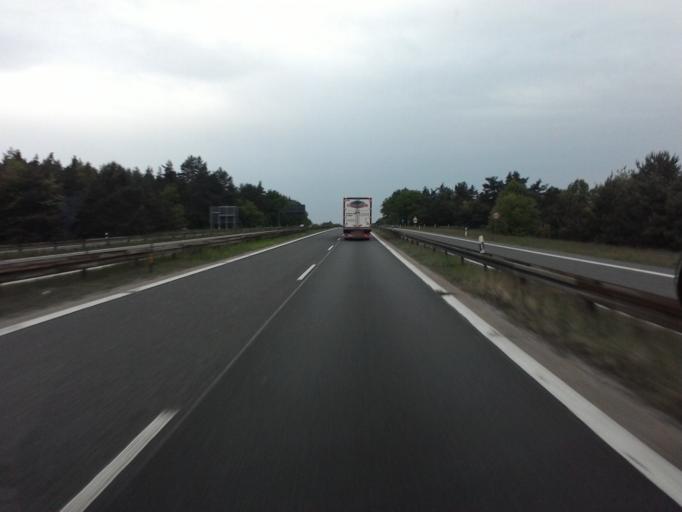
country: DE
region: Bavaria
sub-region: Regierungsbezirk Mittelfranken
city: Rothenbach an der Pegnitz
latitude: 49.4572
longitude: 11.2476
